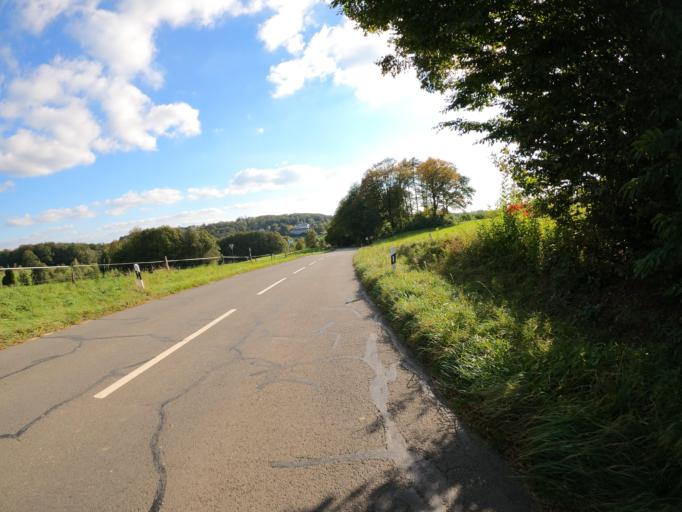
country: DE
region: North Rhine-Westphalia
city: Radevormwald
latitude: 51.2181
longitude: 7.3503
